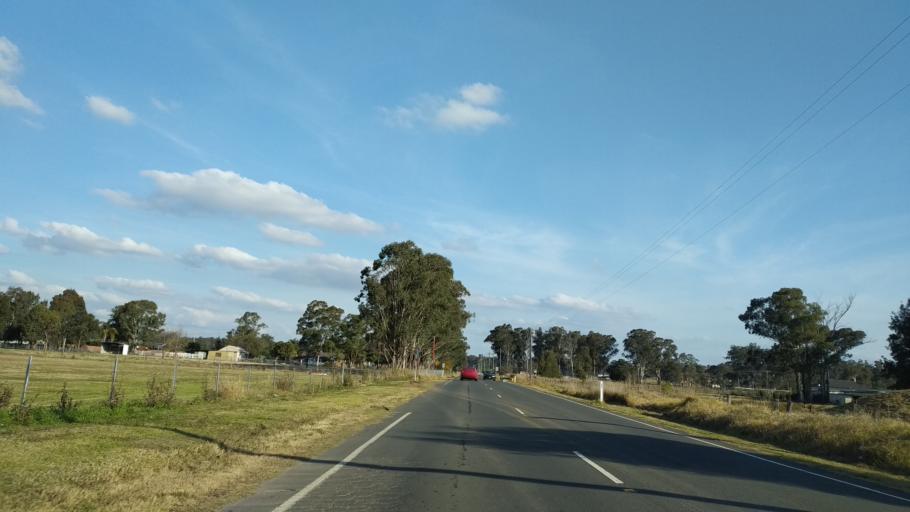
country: AU
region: New South Wales
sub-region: Penrith Municipality
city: Werrington County
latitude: -33.7062
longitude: 150.7573
